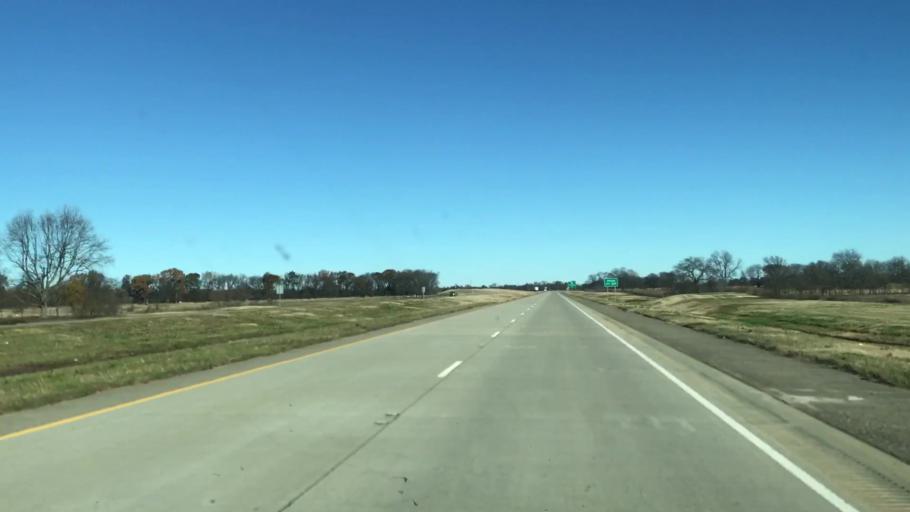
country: US
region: Louisiana
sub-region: Caddo Parish
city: Vivian
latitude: 32.8842
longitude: -93.8602
